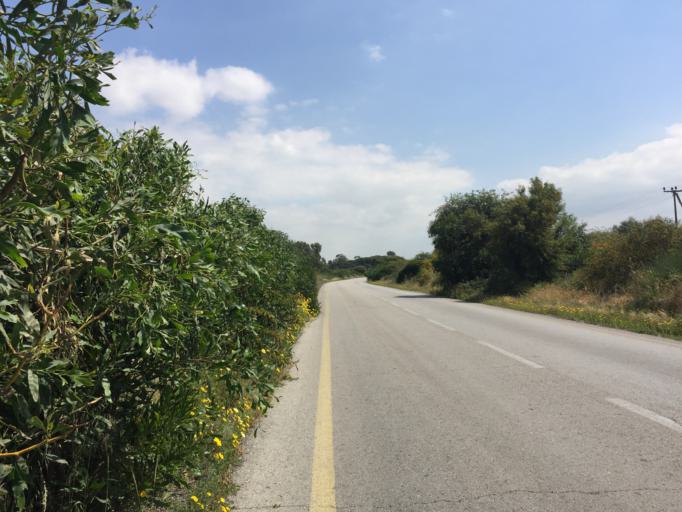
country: IL
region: Haifa
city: Qesarya
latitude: 32.4955
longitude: 34.8953
